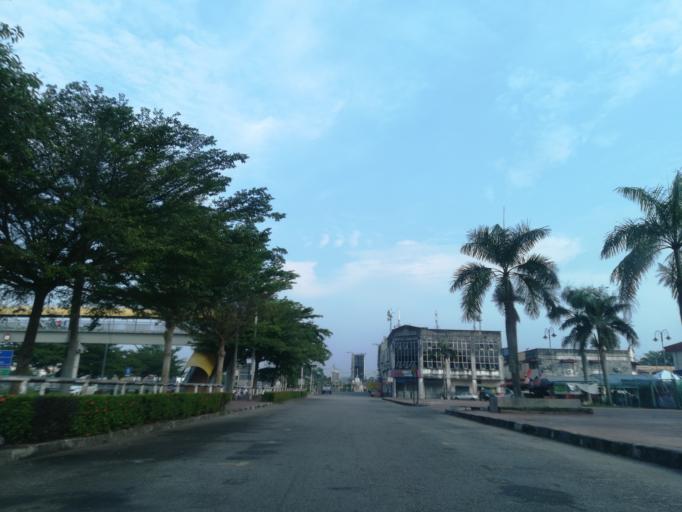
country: MY
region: Kedah
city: Kulim
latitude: 5.3892
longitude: 100.5653
